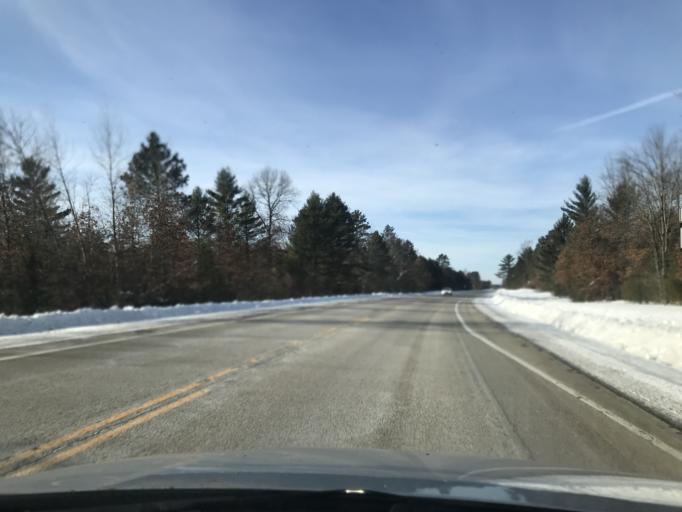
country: US
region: Wisconsin
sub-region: Oconto County
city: Gillett
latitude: 45.1156
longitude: -88.3789
